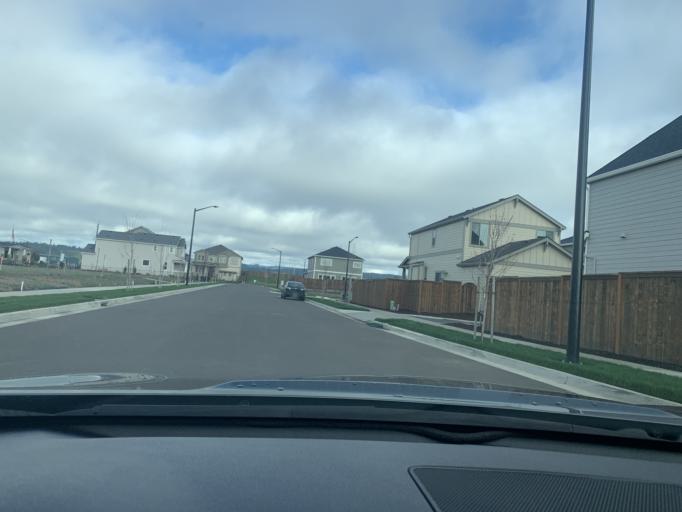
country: US
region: Oregon
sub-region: Washington County
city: North Plains
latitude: 45.5944
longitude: -122.9761
